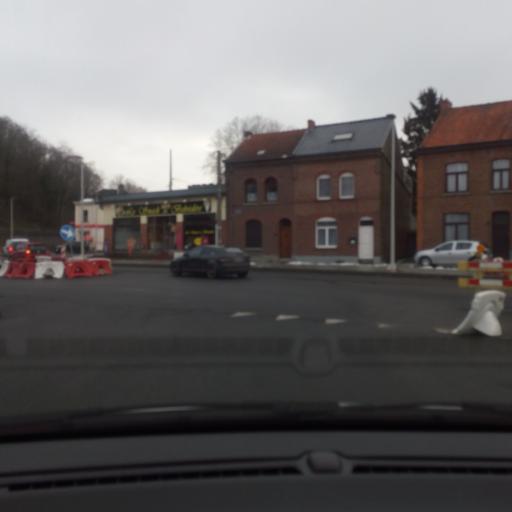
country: BE
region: Wallonia
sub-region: Province du Hainaut
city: Dour
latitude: 50.3947
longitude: 3.7763
